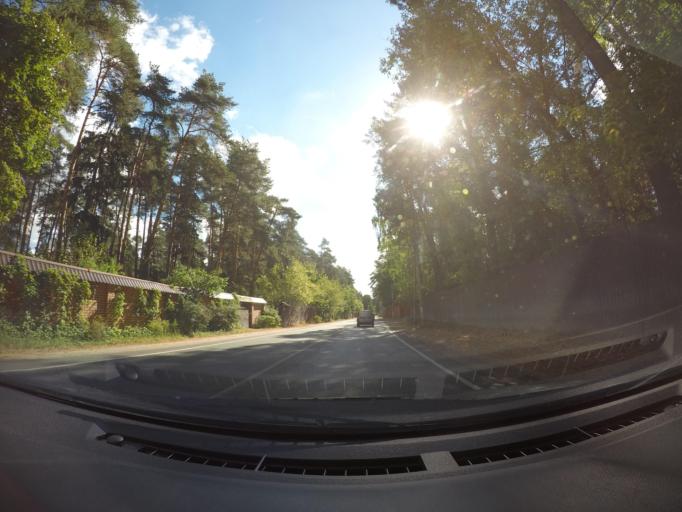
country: RU
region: Moskovskaya
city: Zhukovskiy
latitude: 55.6052
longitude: 38.1469
